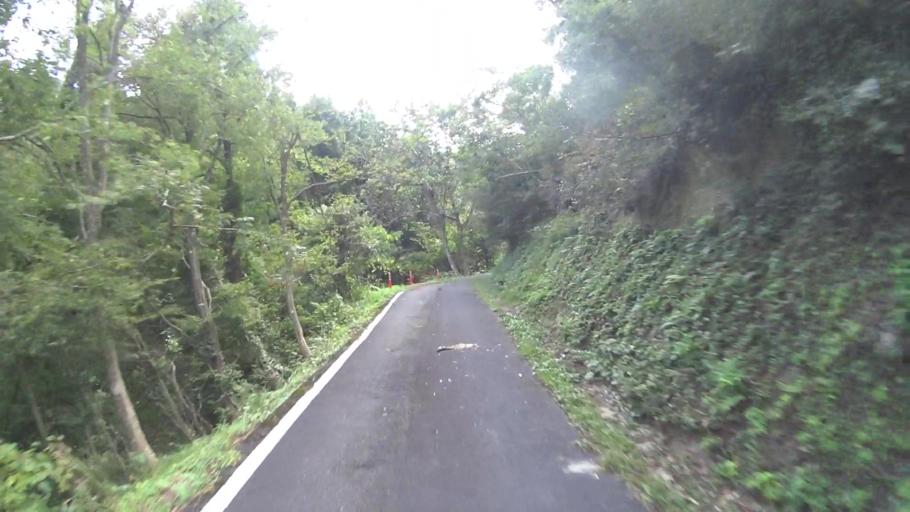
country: JP
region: Kyoto
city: Miyazu
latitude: 35.6715
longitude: 135.1417
